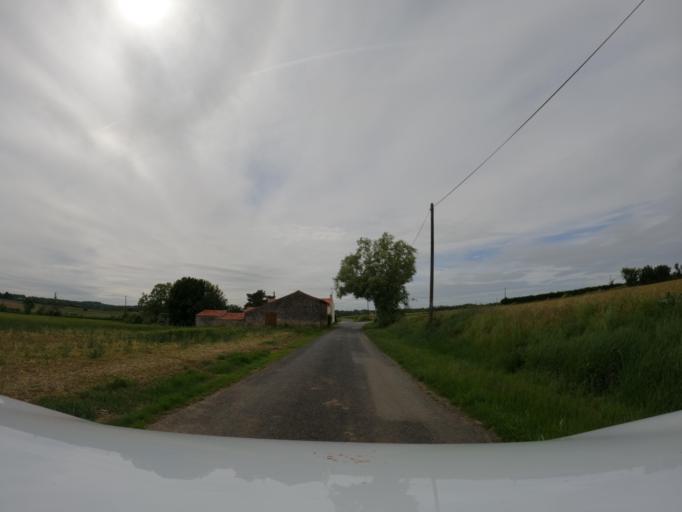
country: FR
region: Pays de la Loire
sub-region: Departement de la Vendee
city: Saint-Hilaire-des-Loges
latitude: 46.5039
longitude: -0.6476
